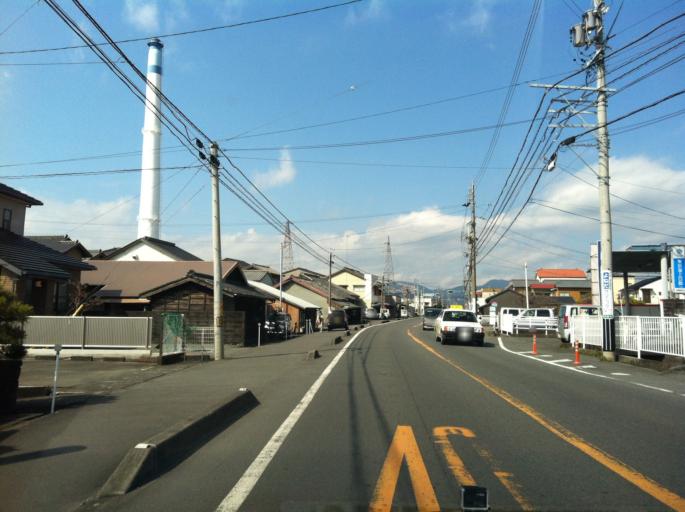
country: JP
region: Shizuoka
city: Shimada
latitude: 34.8331
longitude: 138.1640
